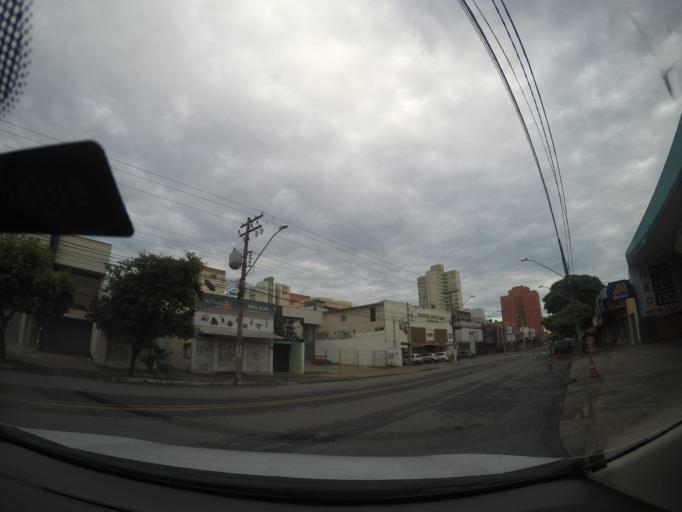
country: BR
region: Goias
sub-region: Goiania
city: Goiania
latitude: -16.6673
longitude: -49.2584
